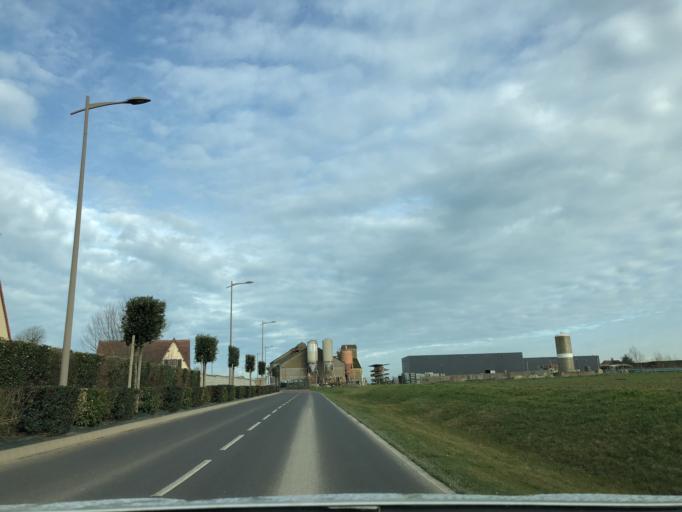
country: FR
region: Lower Normandy
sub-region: Departement du Calvados
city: Douvres-la-Delivrande
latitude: 49.2928
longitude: -0.3680
